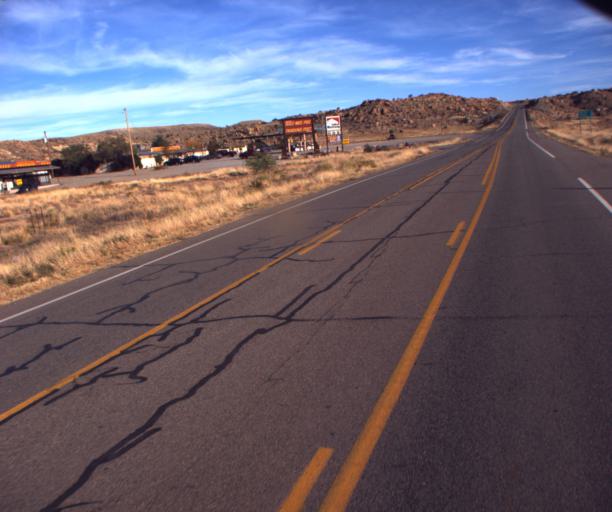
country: US
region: New Mexico
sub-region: San Juan County
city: Shiprock
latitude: 36.9200
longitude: -109.0858
